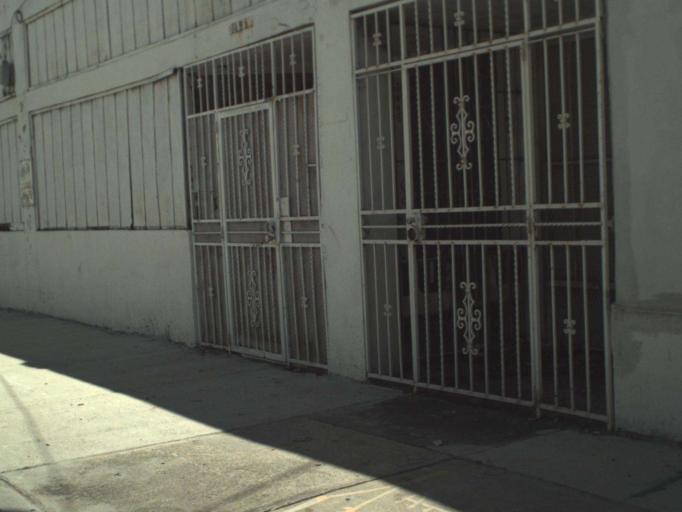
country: US
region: Florida
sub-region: Miami-Dade County
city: Miami
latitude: 25.7894
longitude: -80.2069
